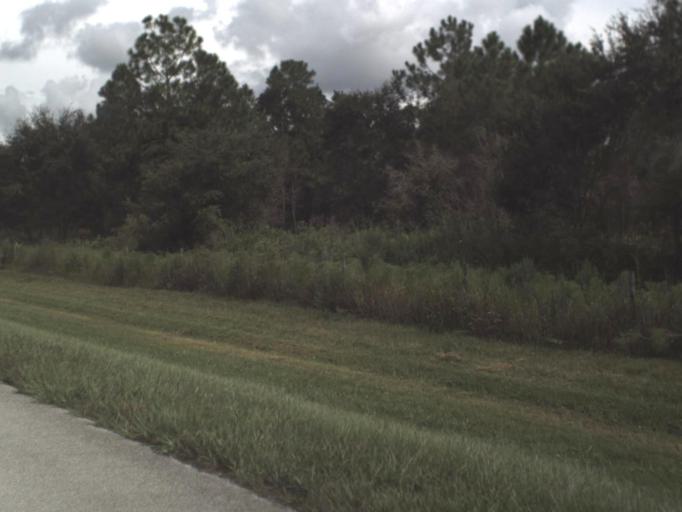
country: US
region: Florida
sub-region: DeSoto County
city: Nocatee
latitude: 27.2054
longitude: -82.0264
